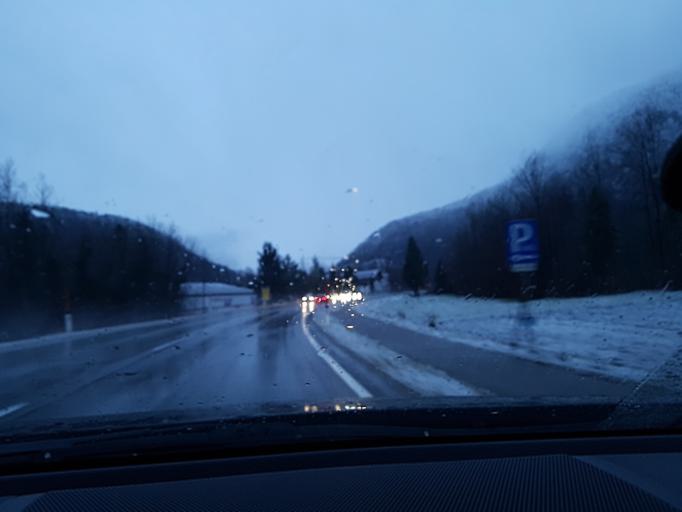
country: AT
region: Upper Austria
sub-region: Politischer Bezirk Gmunden
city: Bad Ischl
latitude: 47.6855
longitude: 13.6257
